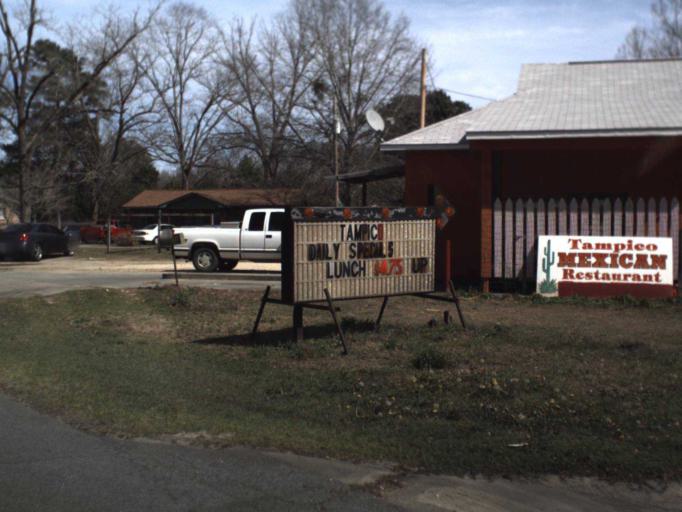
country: US
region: Florida
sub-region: Jackson County
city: Graceville
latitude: 30.9669
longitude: -85.5126
